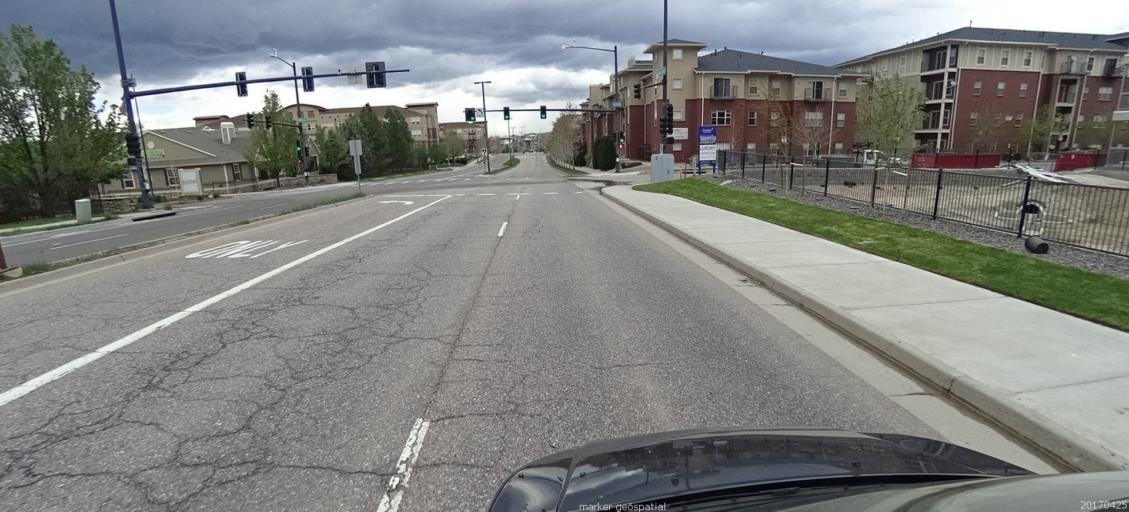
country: US
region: Colorado
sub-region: Douglas County
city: Meridian
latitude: 39.5478
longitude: -104.8719
